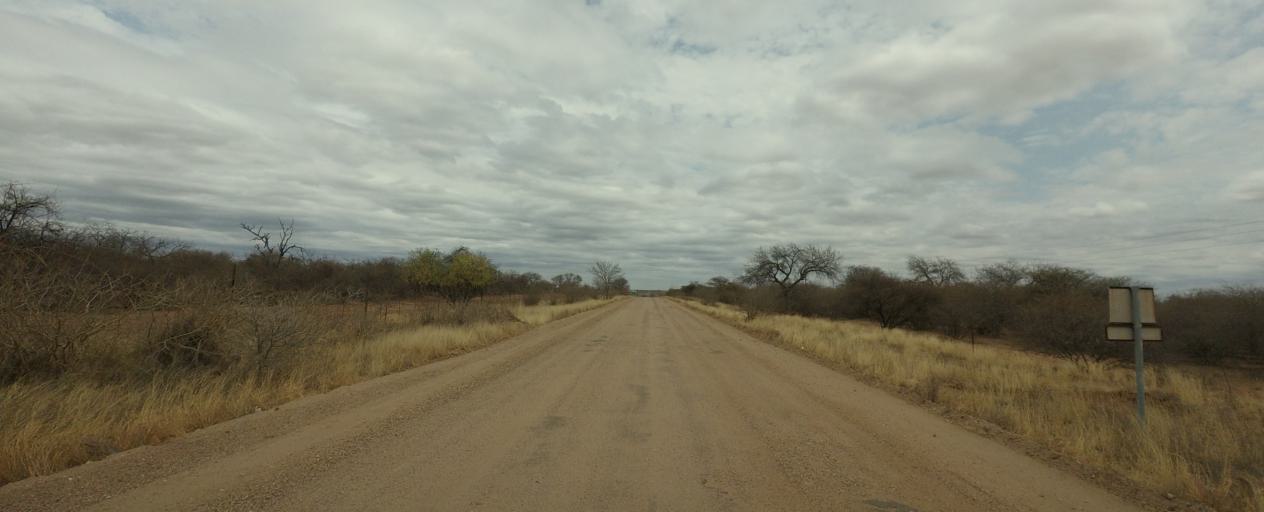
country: BW
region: Central
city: Mathathane
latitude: -22.6798
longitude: 28.6619
